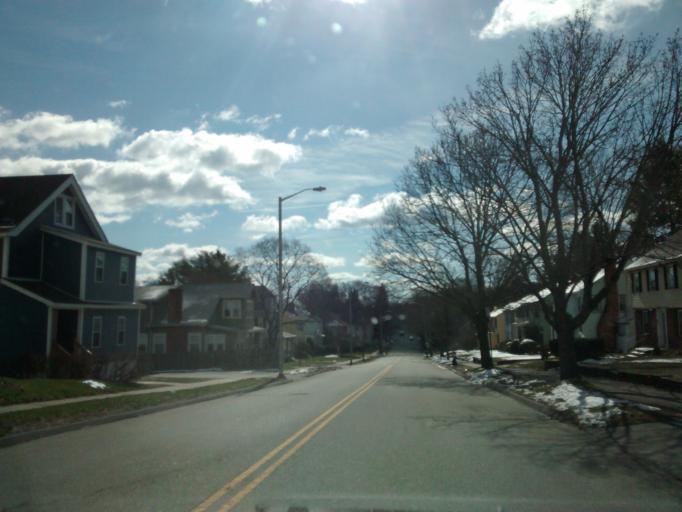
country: US
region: Massachusetts
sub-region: Worcester County
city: Worcester
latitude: 42.2649
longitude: -71.8388
